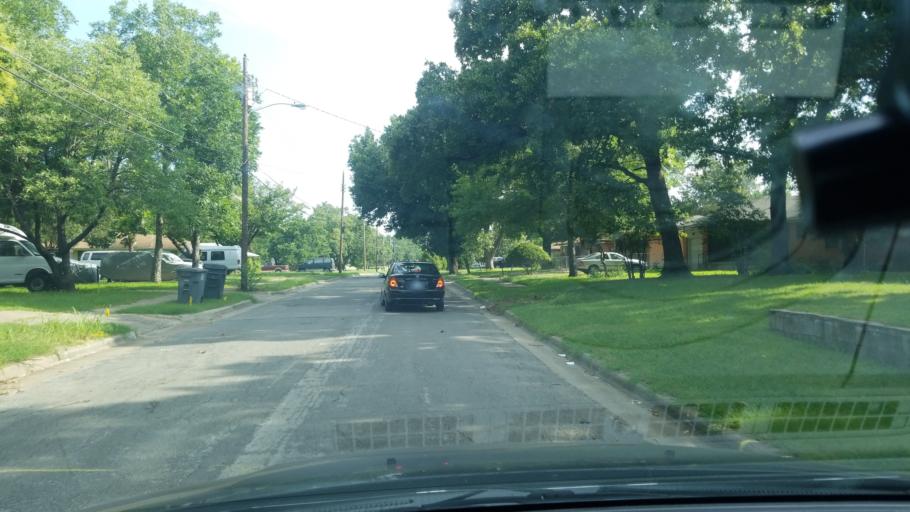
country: US
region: Texas
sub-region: Dallas County
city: Hutchins
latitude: 32.7147
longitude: -96.6915
